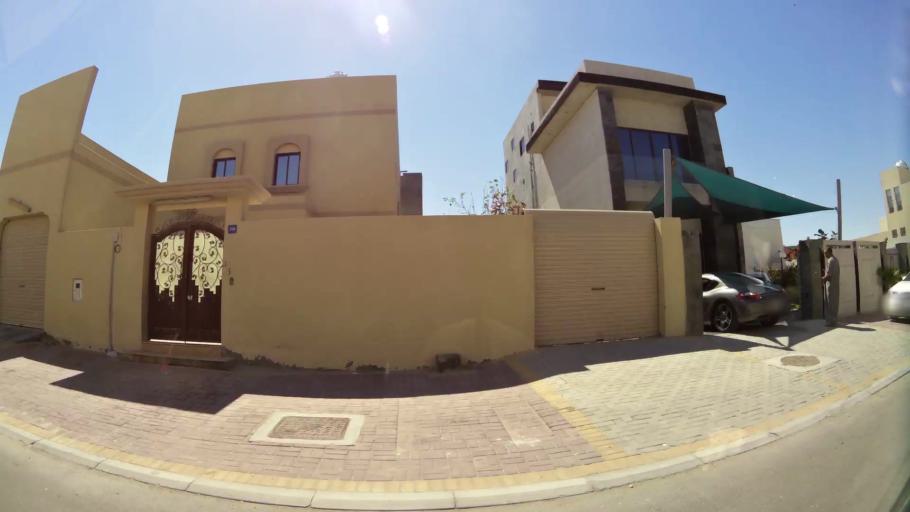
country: BH
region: Muharraq
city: Al Muharraq
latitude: 26.2833
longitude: 50.6373
